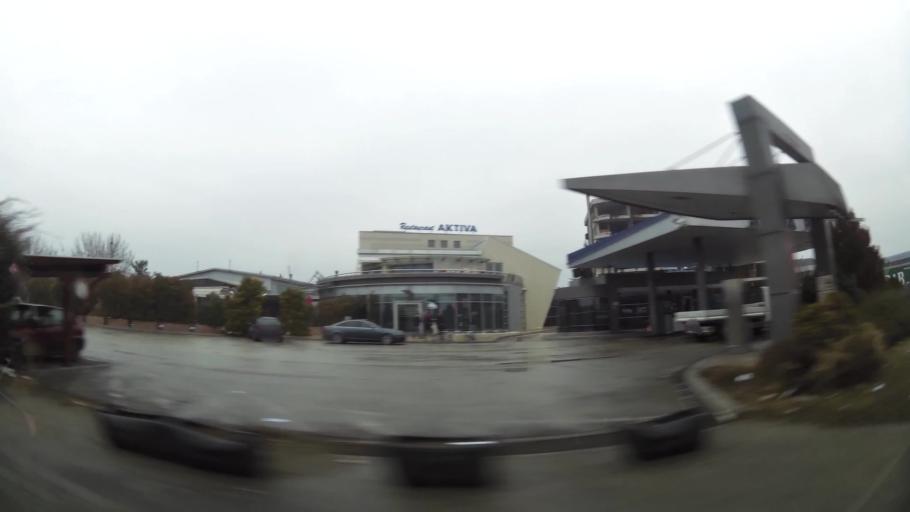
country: MK
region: Suto Orizari
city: Suto Orizare
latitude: 42.0438
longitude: 21.3901
